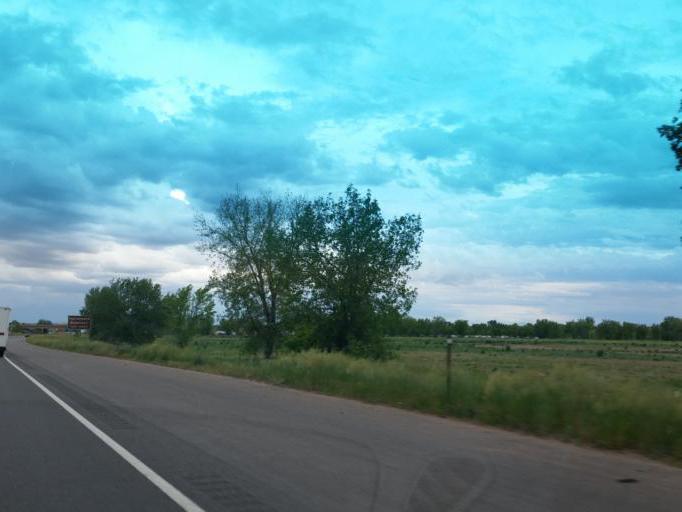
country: US
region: Colorado
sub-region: Weld County
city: Windsor
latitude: 40.5303
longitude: -104.9933
